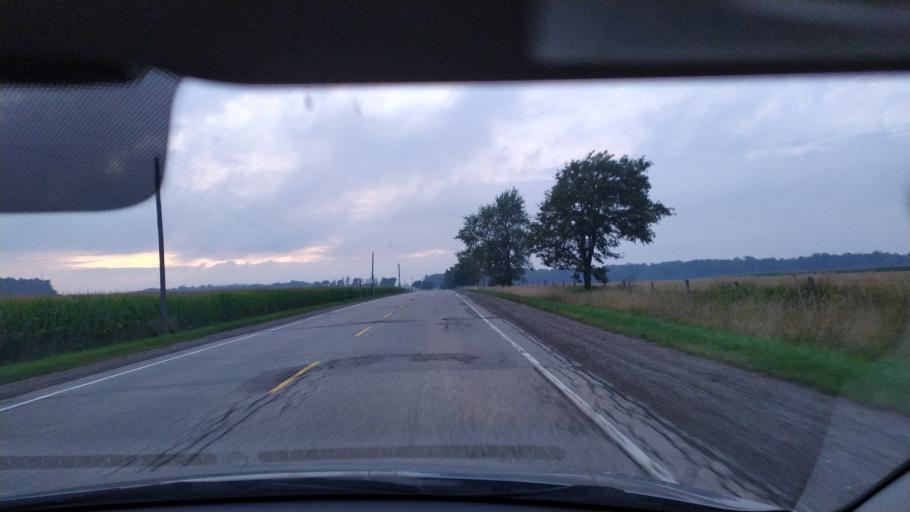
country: CA
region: Ontario
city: Kitchener
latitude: 43.3523
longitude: -80.6974
